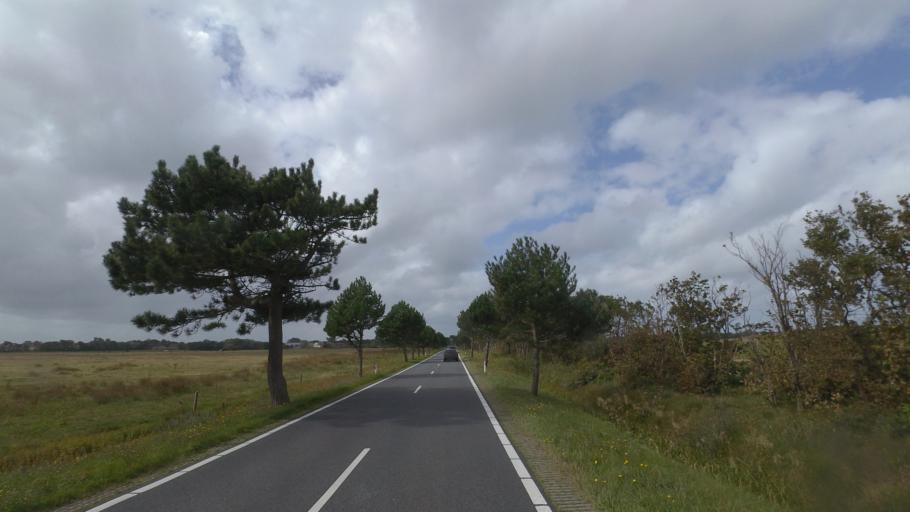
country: NL
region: Friesland
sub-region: Gemeente Ameland
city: Hollum
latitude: 53.4457
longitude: 5.6515
